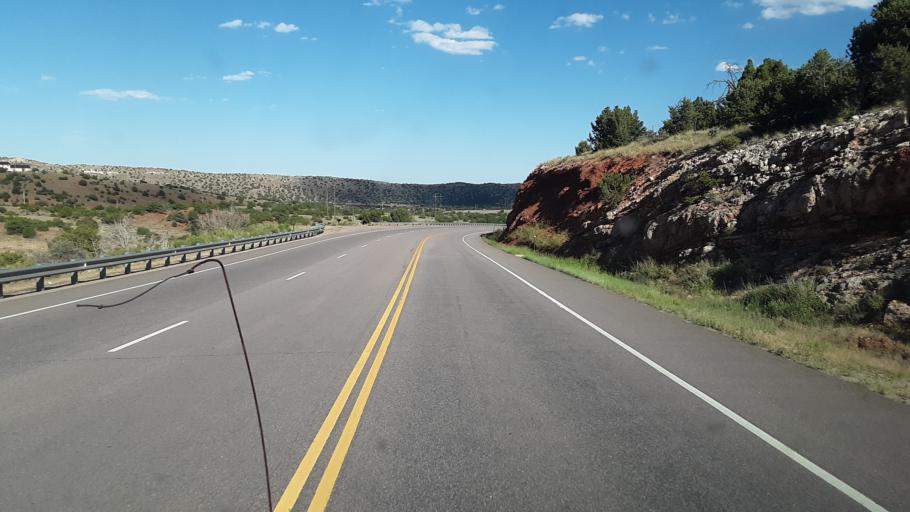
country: US
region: Colorado
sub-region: Fremont County
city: Canon City
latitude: 38.4921
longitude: -105.2823
